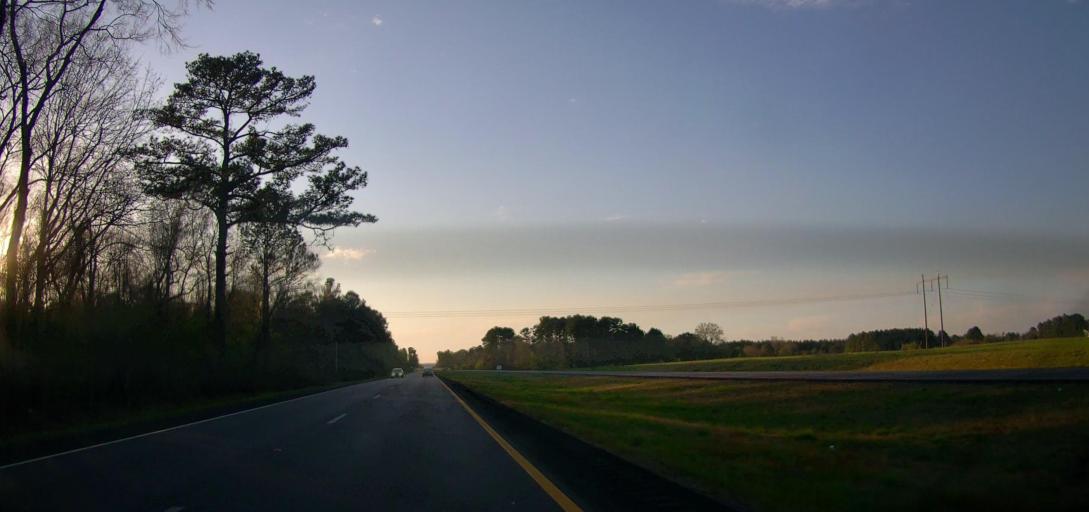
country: US
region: Alabama
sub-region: Shelby County
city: Harpersville
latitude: 33.3296
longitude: -86.4145
